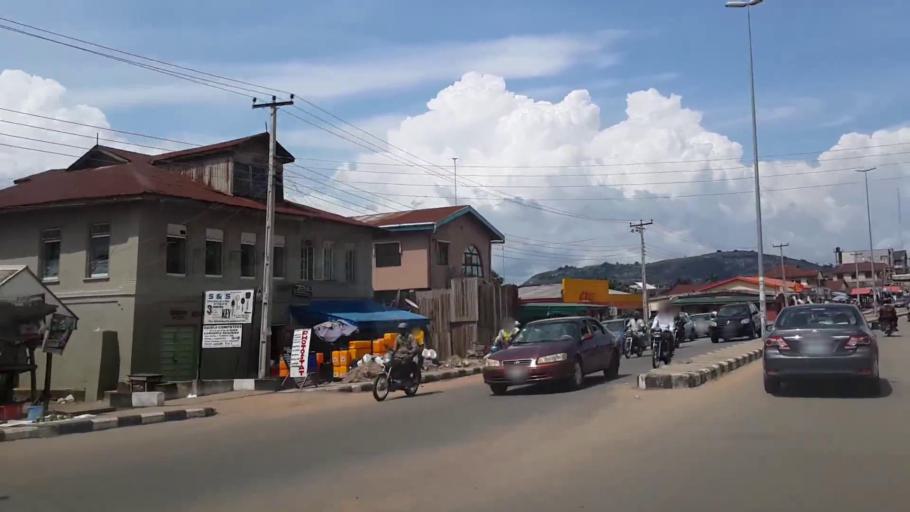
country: NG
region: Ondo
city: Ondo
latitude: 7.0988
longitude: 4.8417
